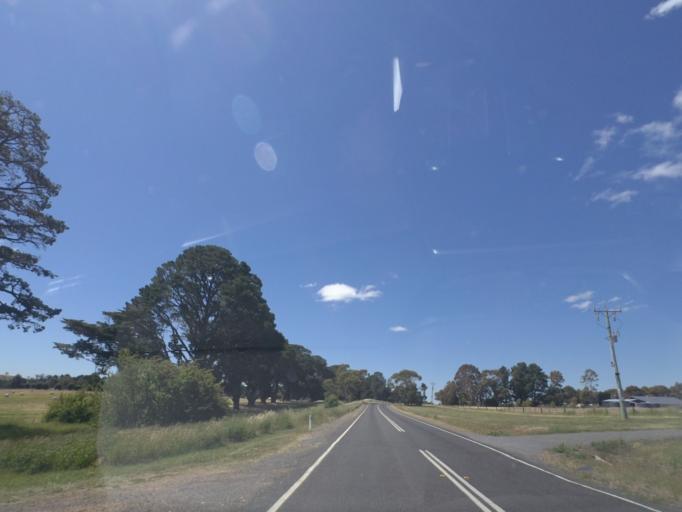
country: AU
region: Victoria
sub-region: Mount Alexander
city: Castlemaine
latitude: -37.2334
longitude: 144.3305
